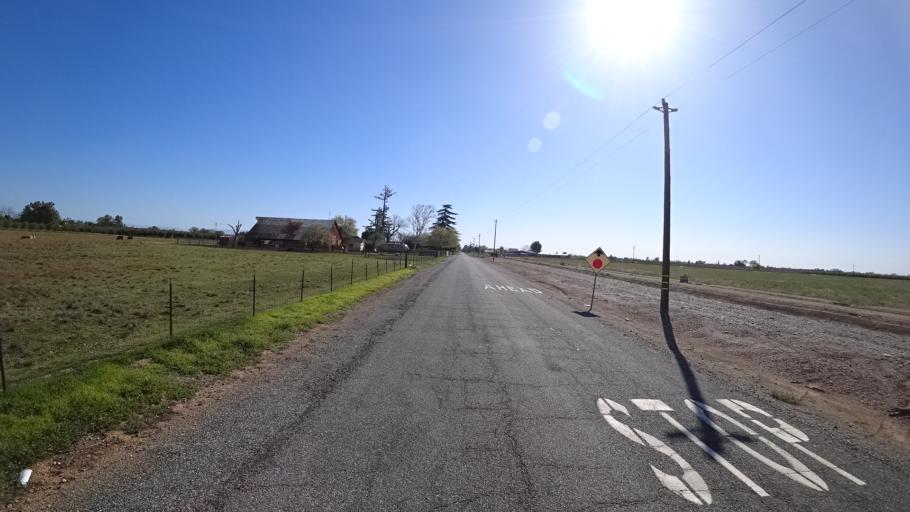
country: US
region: California
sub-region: Glenn County
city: Orland
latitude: 39.7442
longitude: -122.2411
